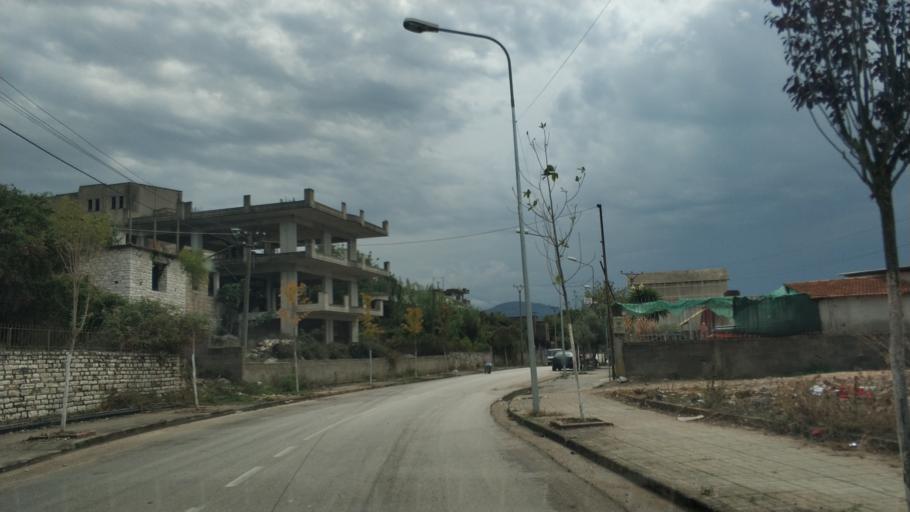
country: AL
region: Vlore
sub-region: Rrethi i Sarandes
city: Sarande
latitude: 39.8451
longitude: 20.0337
